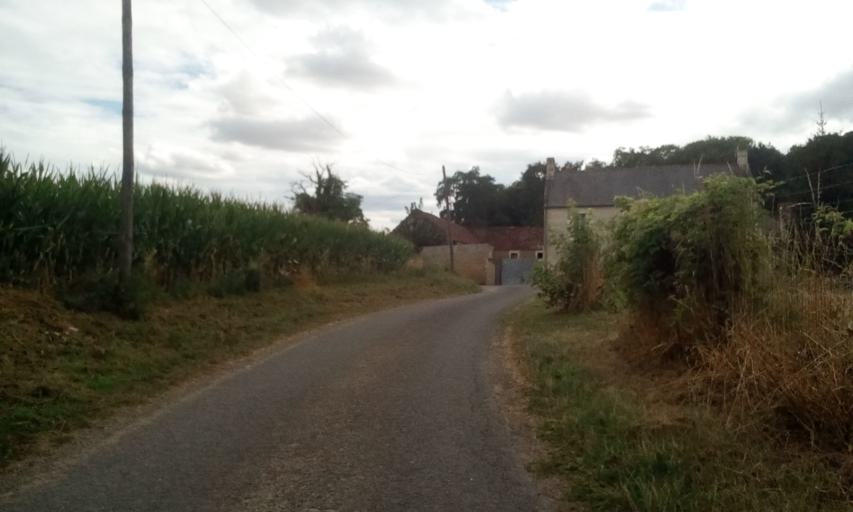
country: FR
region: Lower Normandy
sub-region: Departement du Calvados
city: Bellengreville
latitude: 49.1294
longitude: -0.1936
